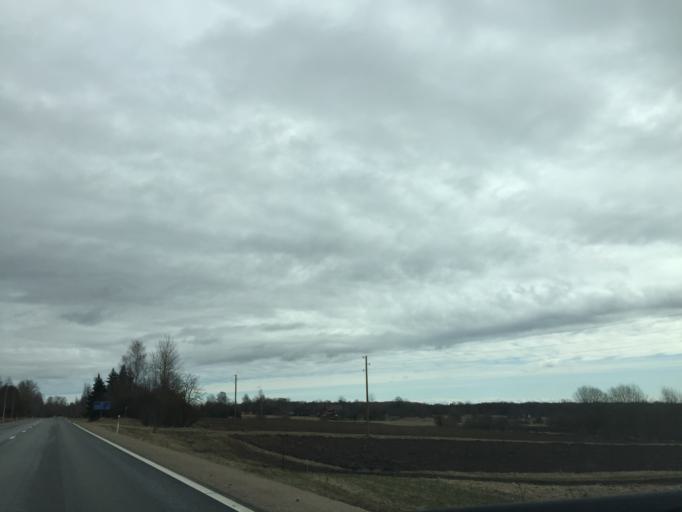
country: LV
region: Daugavpils
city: Daugavpils
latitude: 55.9284
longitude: 26.6937
